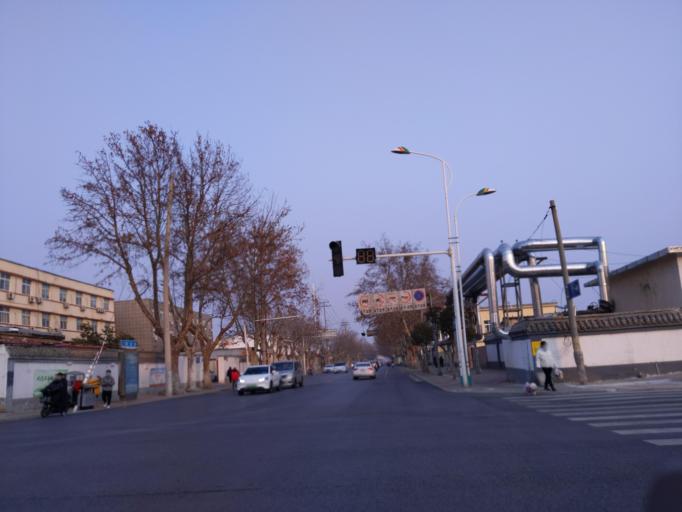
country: CN
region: Henan Sheng
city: Zhongyuanlu
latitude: 35.7864
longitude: 115.0622
